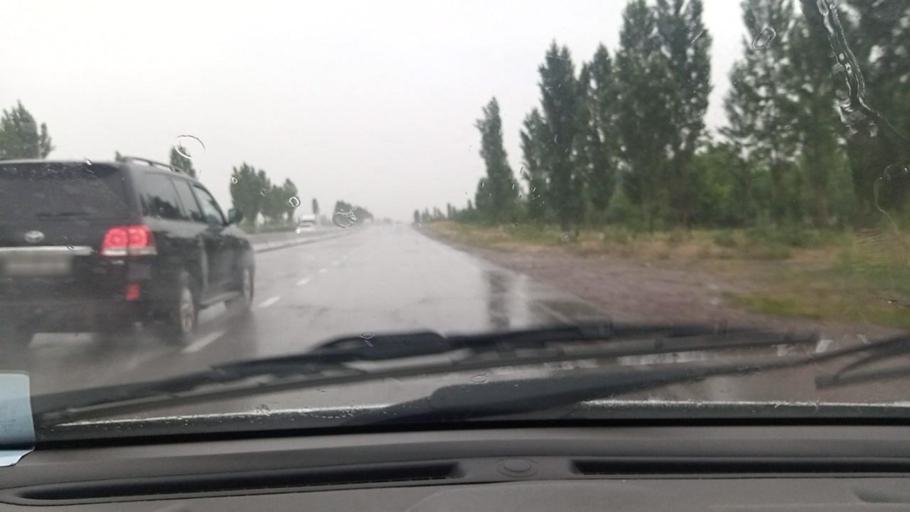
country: UZ
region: Toshkent
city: Ohangaron
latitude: 40.9125
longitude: 69.8186
